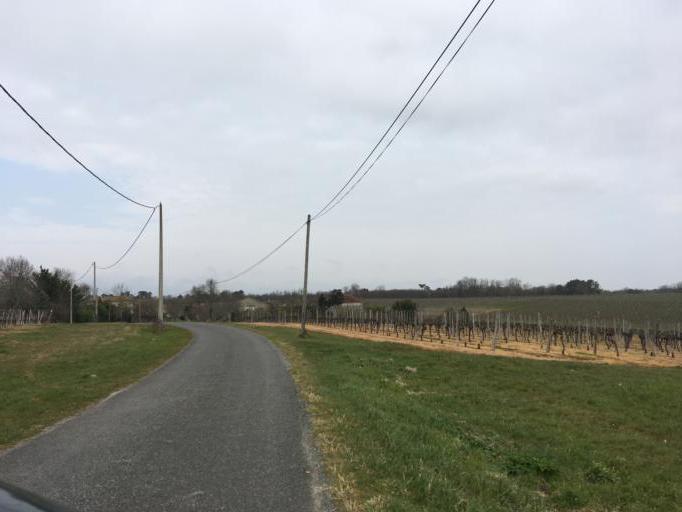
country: FR
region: Poitou-Charentes
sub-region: Departement de la Charente-Maritime
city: Mirambeau
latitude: 45.3335
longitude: -0.5796
